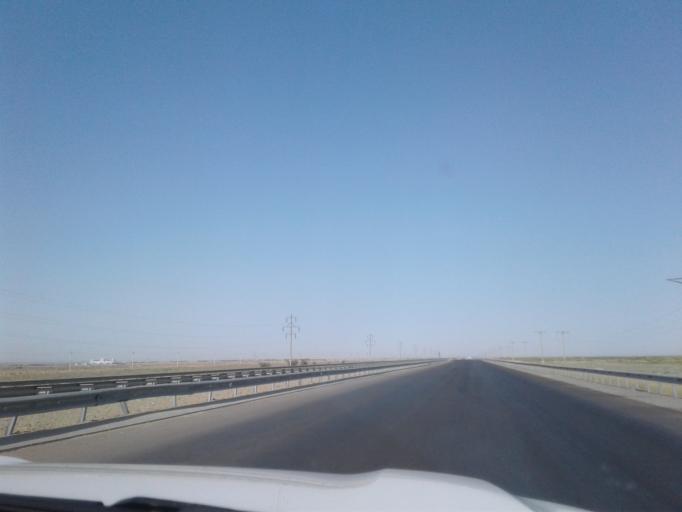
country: TM
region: Balkan
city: Gazanjyk
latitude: 39.2715
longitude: 55.5157
